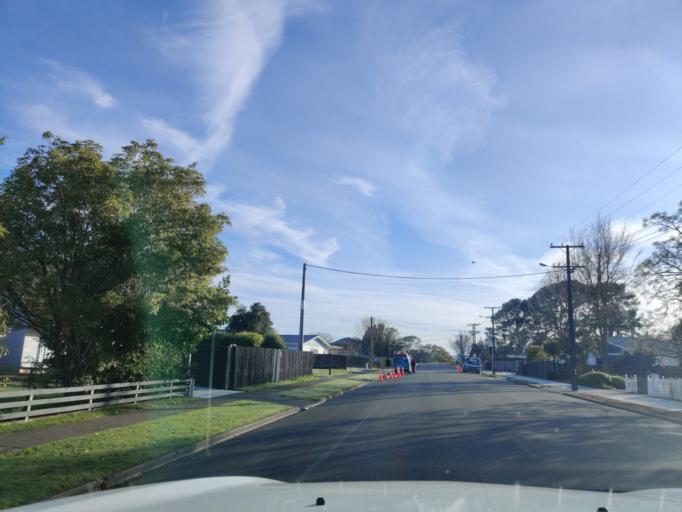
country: NZ
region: Manawatu-Wanganui
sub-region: Palmerston North City
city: Palmerston North
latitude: -40.2832
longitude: 175.7601
